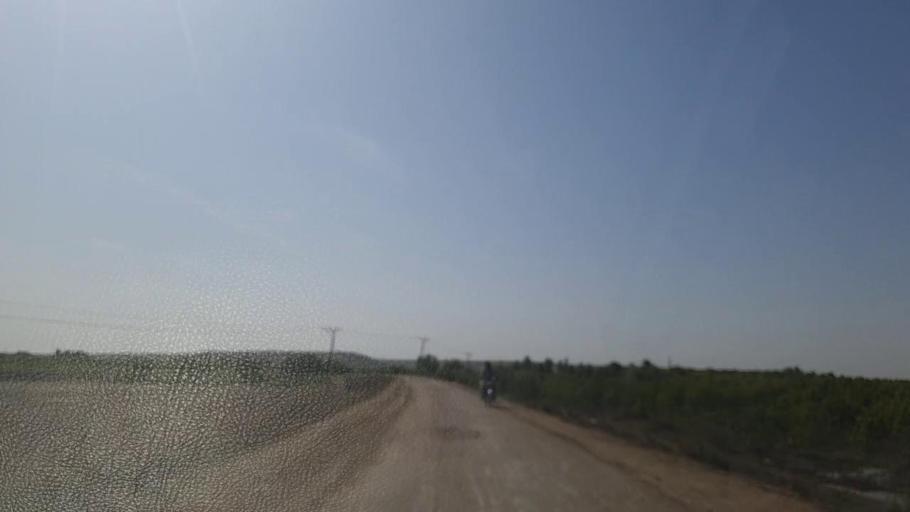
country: PK
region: Sindh
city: Thatta
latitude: 24.6405
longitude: 67.8816
